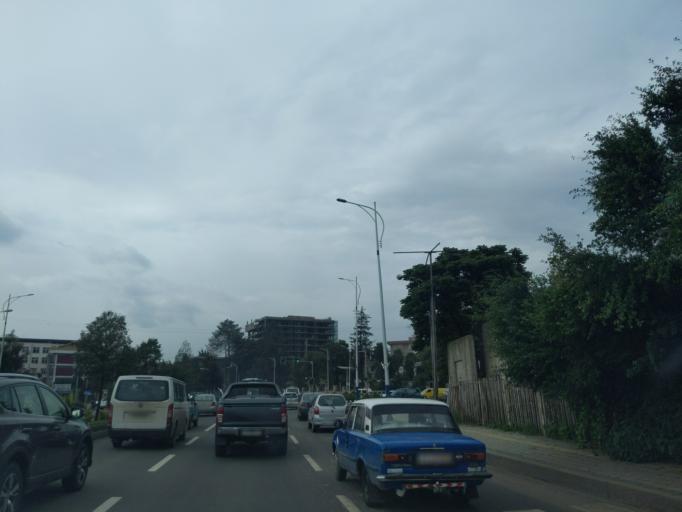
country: ET
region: Adis Abeba
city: Addis Ababa
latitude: 9.0289
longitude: 38.7634
